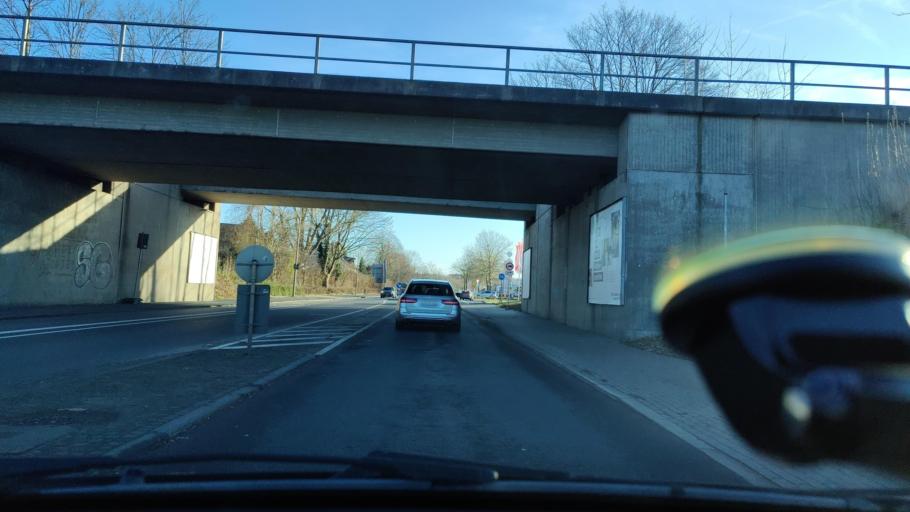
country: DE
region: North Rhine-Westphalia
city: Castrop-Rauxel
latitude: 51.5568
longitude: 7.2933
